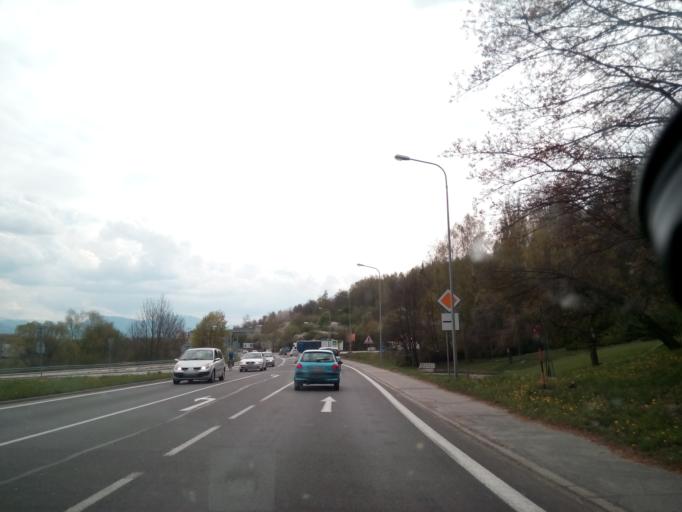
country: SK
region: Zilinsky
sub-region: Okres Zilina
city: Vrutky
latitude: 49.1062
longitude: 18.9177
